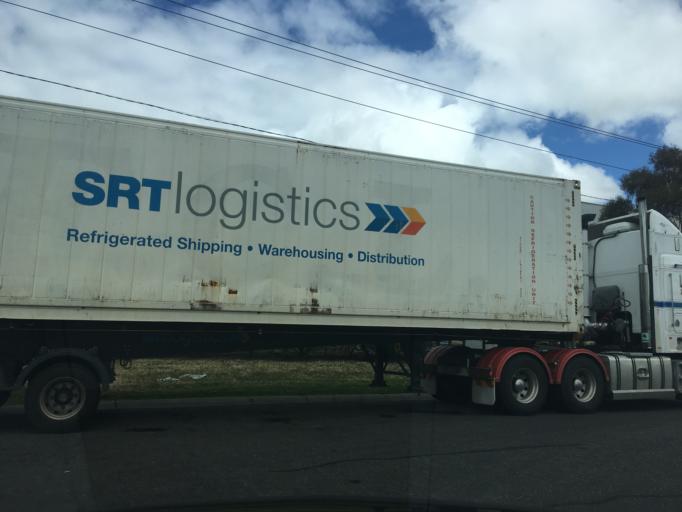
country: AU
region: Victoria
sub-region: Brimbank
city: Sunshine West
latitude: -37.8182
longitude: 144.7968
